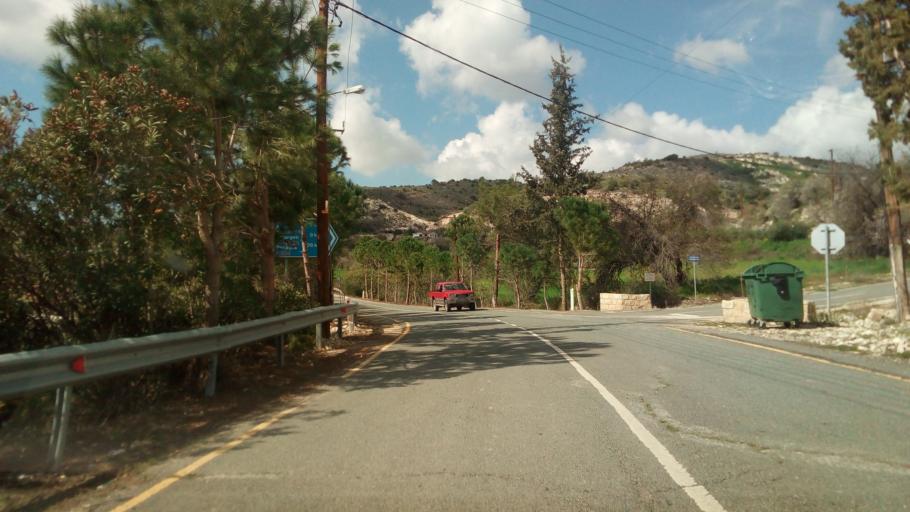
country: CY
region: Pafos
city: Mesogi
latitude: 34.7817
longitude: 32.5667
